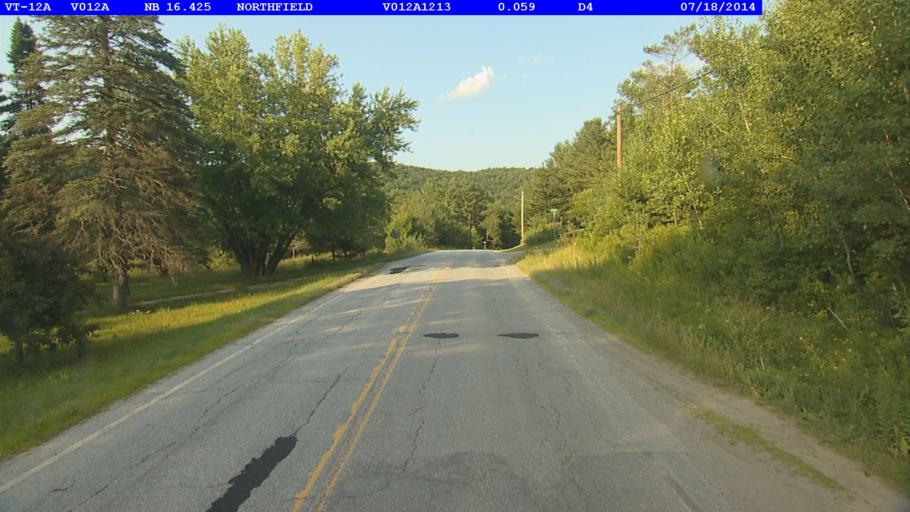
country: US
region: Vermont
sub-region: Washington County
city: Northfield
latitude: 44.1145
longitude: -72.7235
